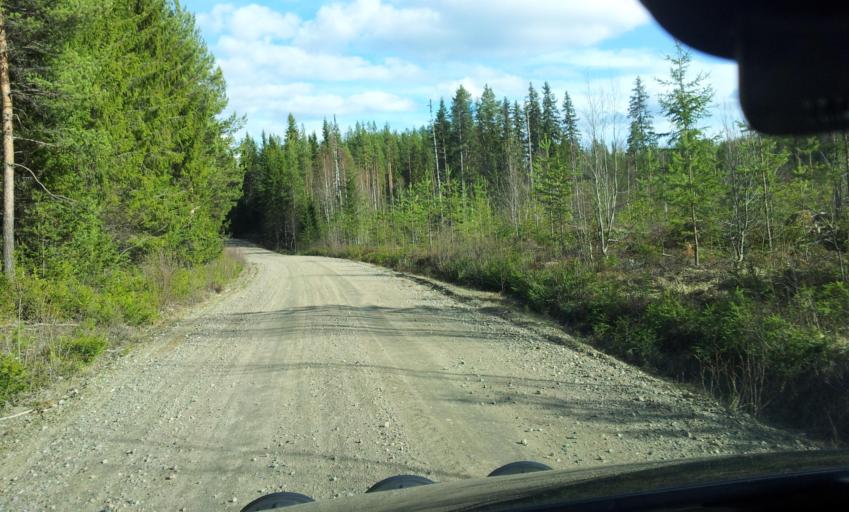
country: SE
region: Vaesternorrland
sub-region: Ange Kommun
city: Ange
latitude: 62.1823
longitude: 15.6189
